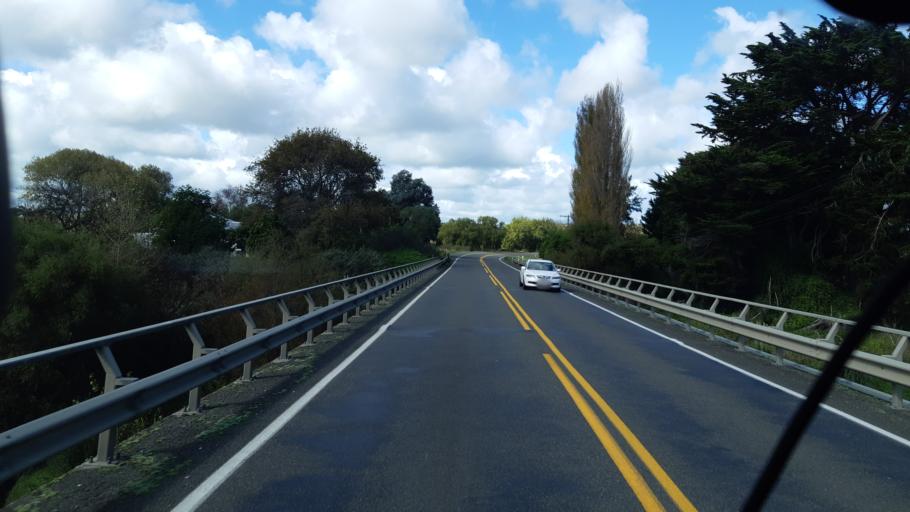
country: NZ
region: Manawatu-Wanganui
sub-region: Wanganui District
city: Wanganui
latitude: -40.0333
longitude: 175.2084
